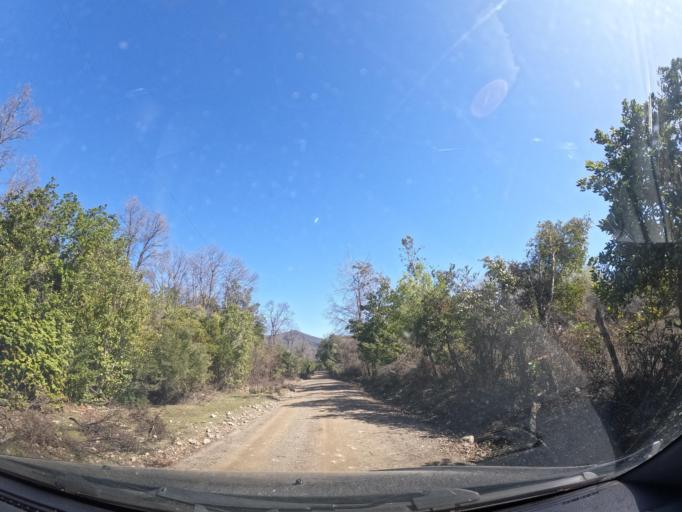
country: CL
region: Maule
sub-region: Provincia de Linares
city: Longavi
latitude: -36.2470
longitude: -71.3352
